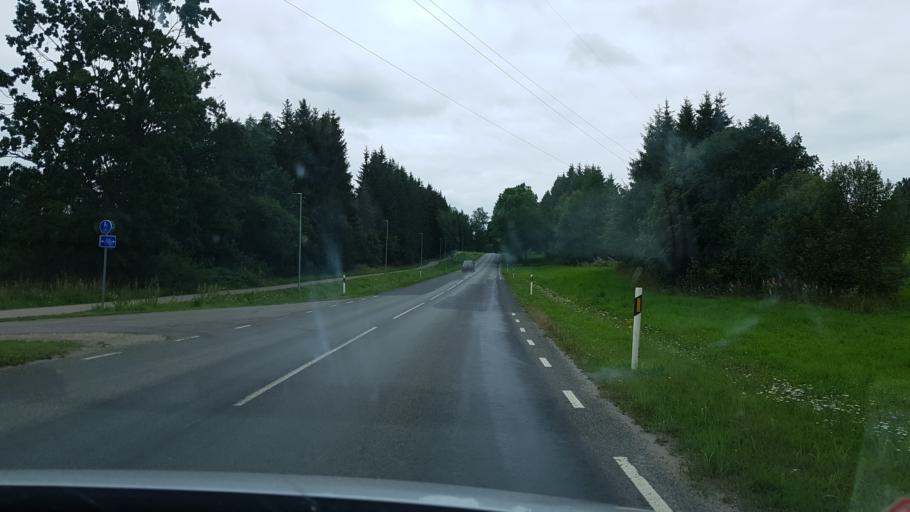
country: EE
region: Vorumaa
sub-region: Antsla vald
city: Vana-Antsla
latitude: 57.9788
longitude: 26.7752
